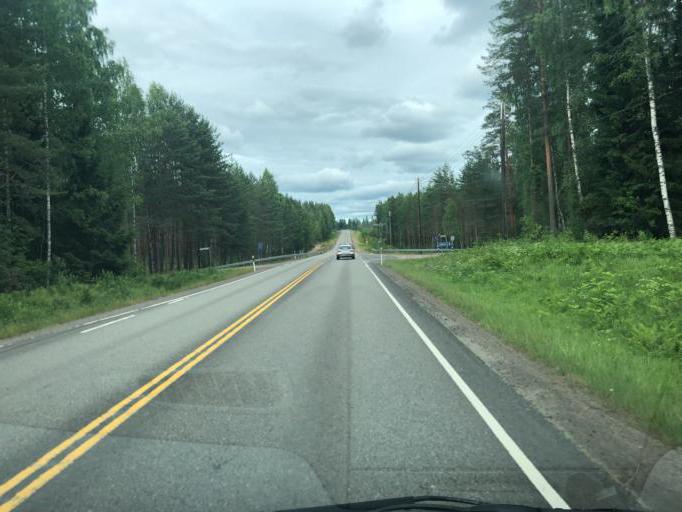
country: FI
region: Kymenlaakso
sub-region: Kouvola
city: Kouvola
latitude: 60.9693
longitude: 26.8905
